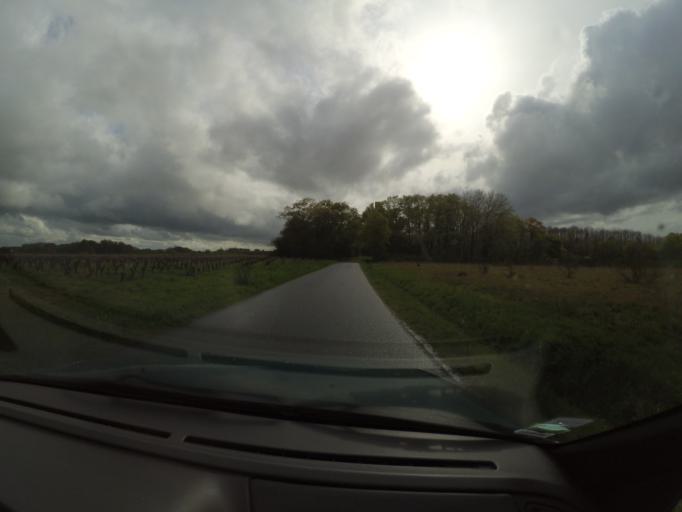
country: FR
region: Pays de la Loire
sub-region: Departement de la Loire-Atlantique
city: Monnieres
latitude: 47.1196
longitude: -1.3578
